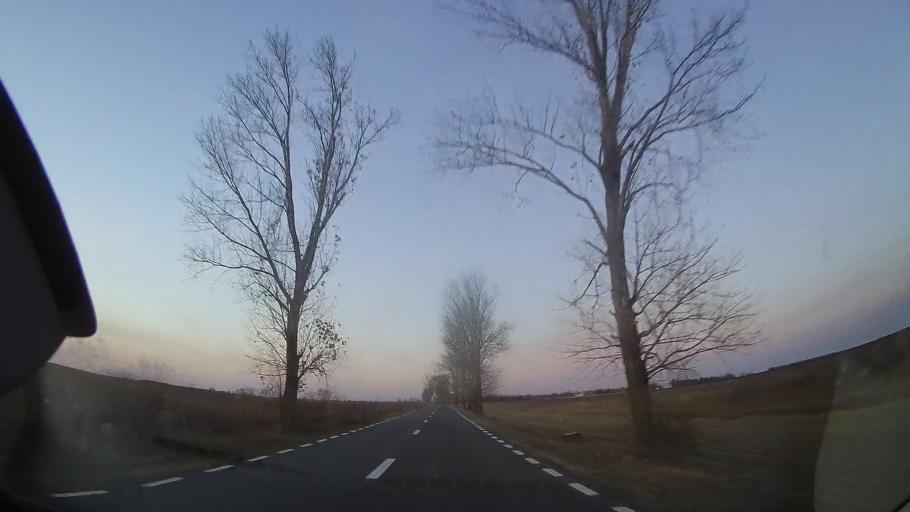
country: RO
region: Constanta
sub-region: Comuna Cobadin
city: Cobadin
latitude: 44.0415
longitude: 28.2560
